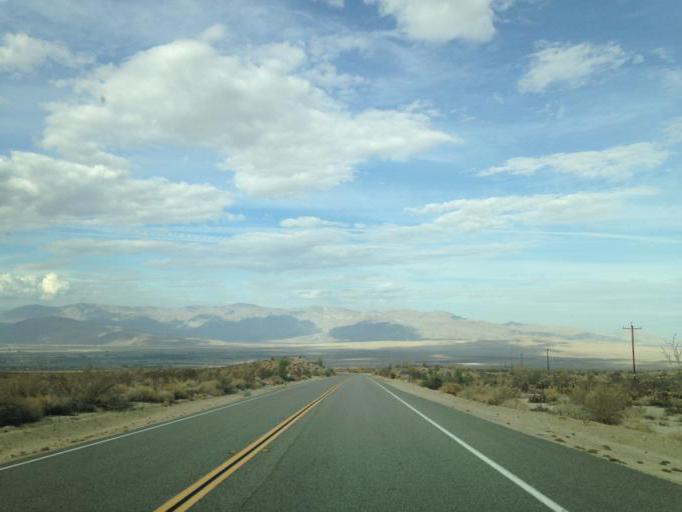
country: US
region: California
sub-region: San Diego County
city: Borrego Springs
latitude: 33.1618
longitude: -116.3373
